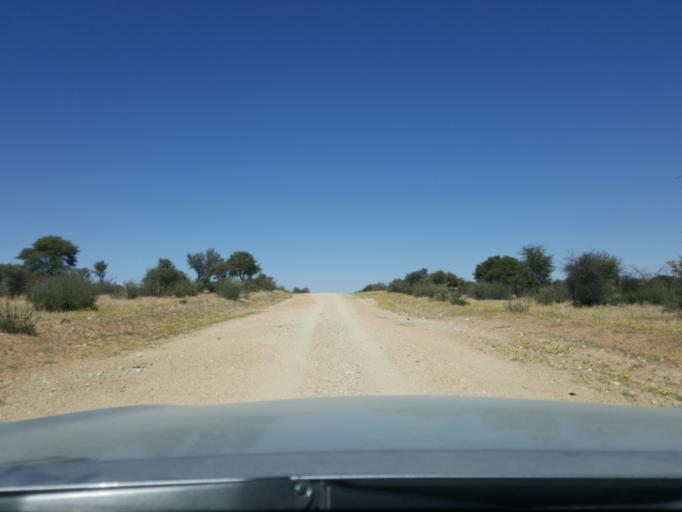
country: BW
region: Kgalagadi
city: Hukuntsi
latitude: -24.0573
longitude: 21.2222
